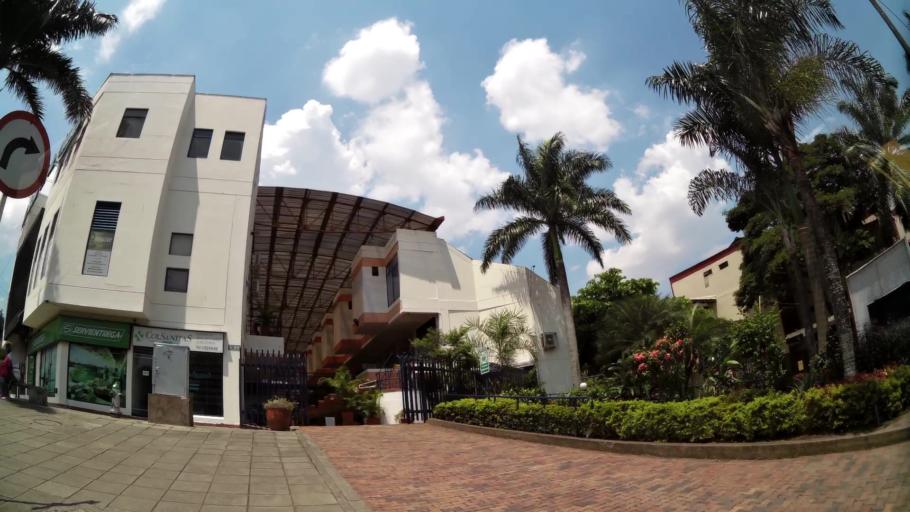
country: CO
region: Valle del Cauca
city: Cali
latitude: 3.4157
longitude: -76.5479
